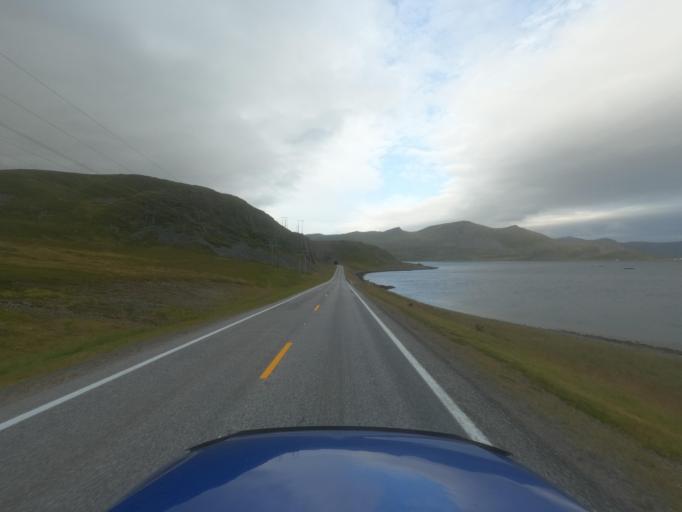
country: NO
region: Finnmark Fylke
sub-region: Nordkapp
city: Honningsvag
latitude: 70.9750
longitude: 25.7060
